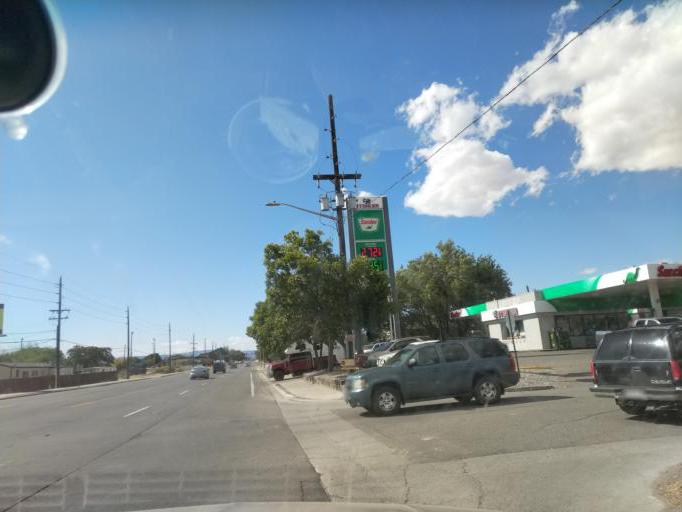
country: US
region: Colorado
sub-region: Mesa County
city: Clifton
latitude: 39.0919
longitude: -108.4552
